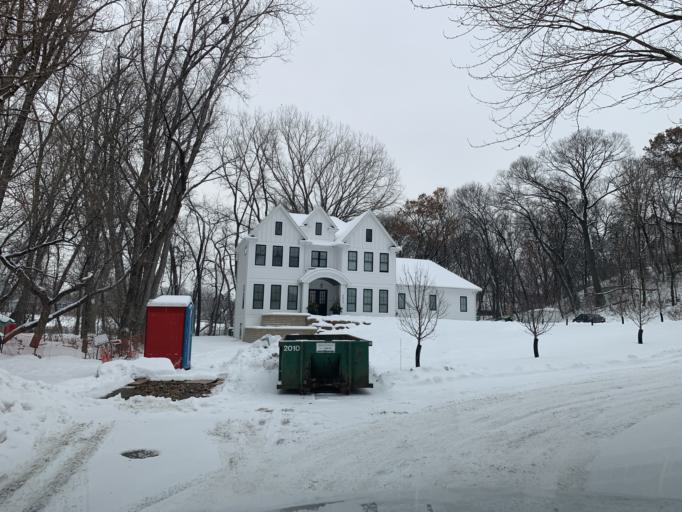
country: US
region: Minnesota
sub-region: Hennepin County
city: Saint Louis Park
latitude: 44.9507
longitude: -93.3383
